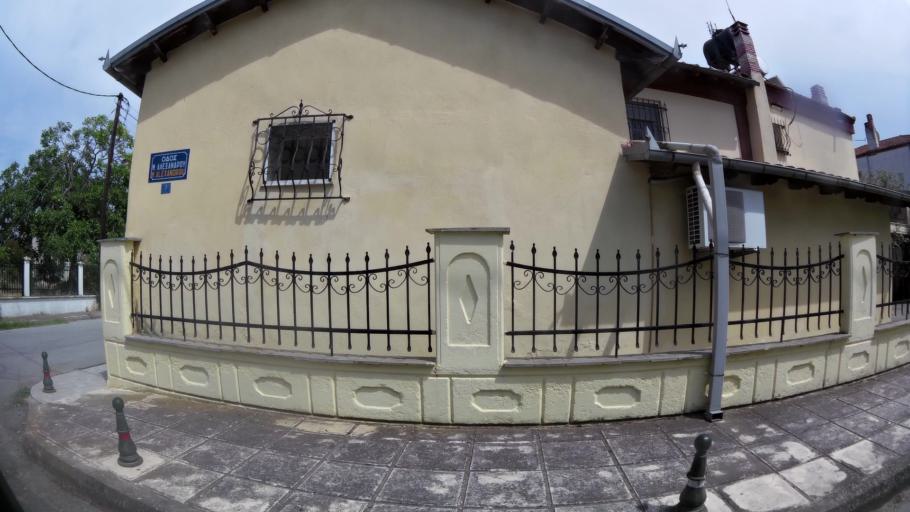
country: GR
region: Central Macedonia
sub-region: Nomos Pierias
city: Korinos
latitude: 40.3185
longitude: 22.5800
